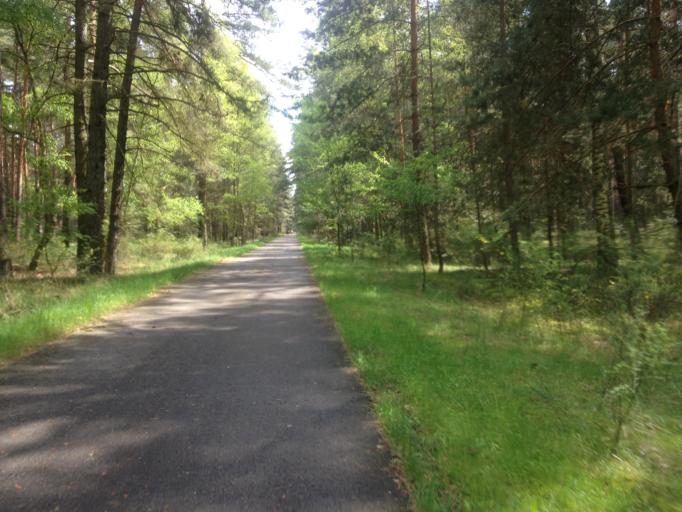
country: DE
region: Brandenburg
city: Briesen
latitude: 51.8073
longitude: 14.2665
